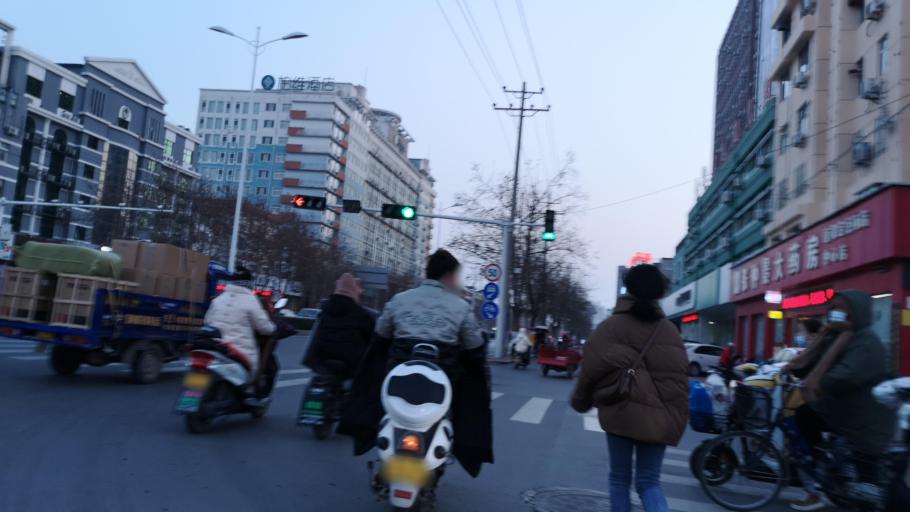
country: CN
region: Henan Sheng
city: Zhongyuanlu
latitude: 35.7690
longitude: 115.0689
